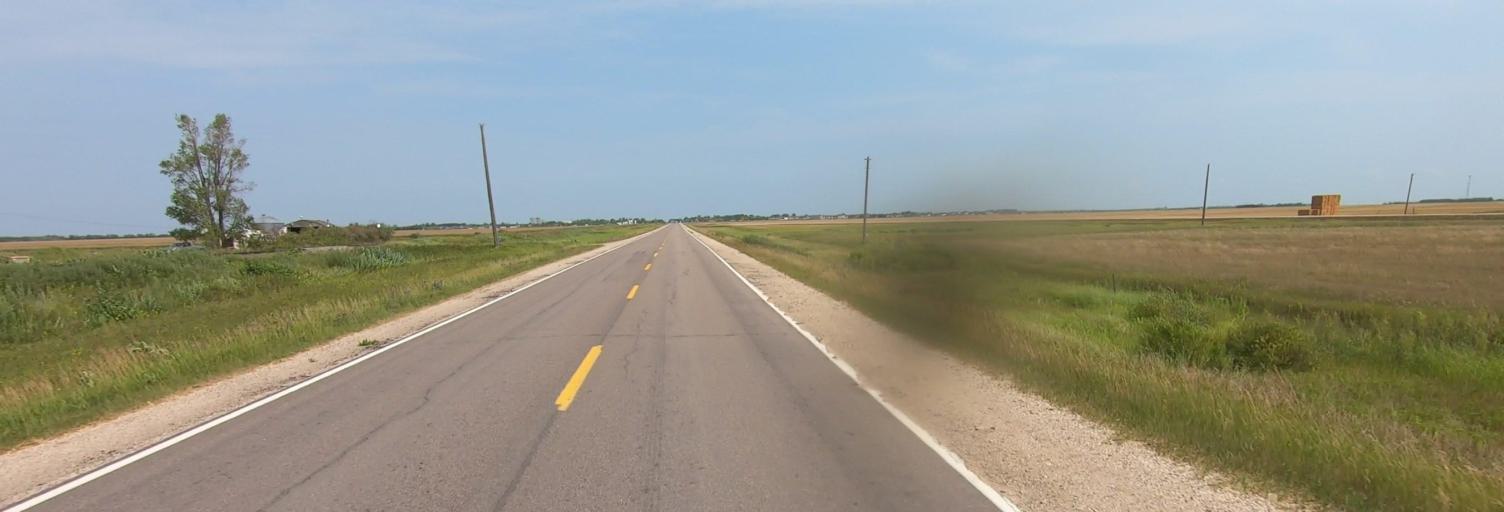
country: CA
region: Manitoba
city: Headingley
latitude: 49.6719
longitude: -97.2793
